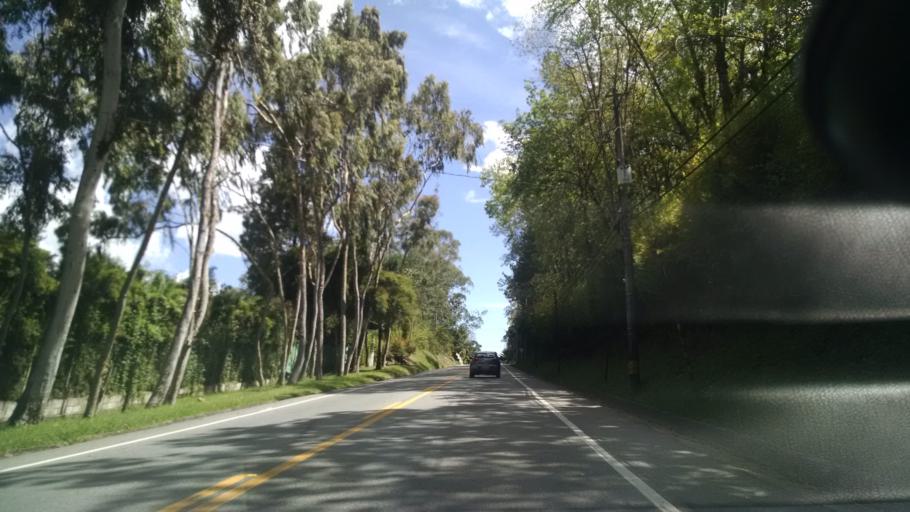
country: CO
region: Antioquia
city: El Retiro
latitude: 6.0970
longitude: -75.5036
